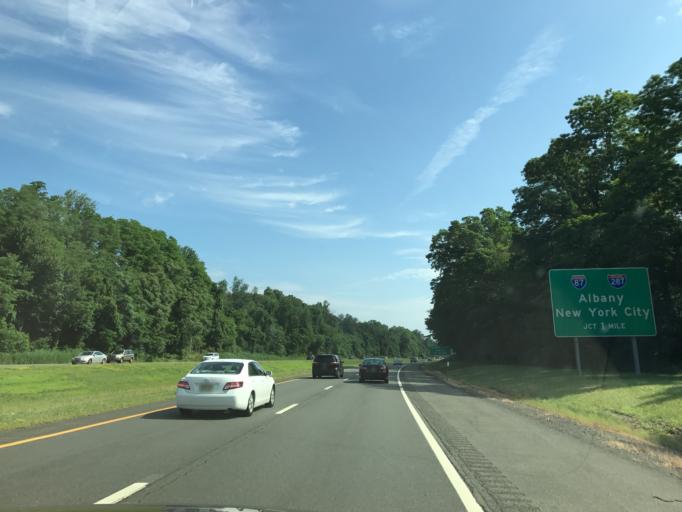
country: US
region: New York
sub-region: Rockland County
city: Chestnut Ridge
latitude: 41.0781
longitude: -74.0497
